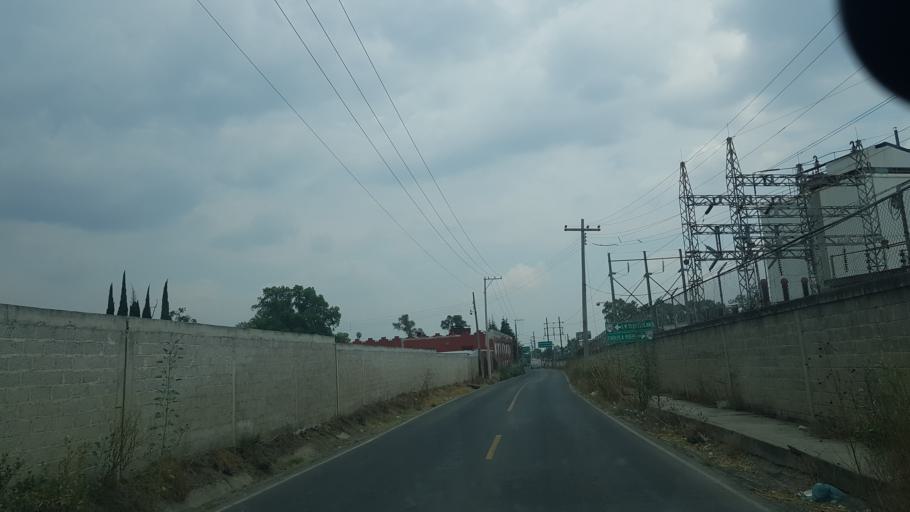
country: MX
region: Puebla
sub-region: Huejotzingo
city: San Mateo Capultitlan
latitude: 19.2021
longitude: -98.4223
